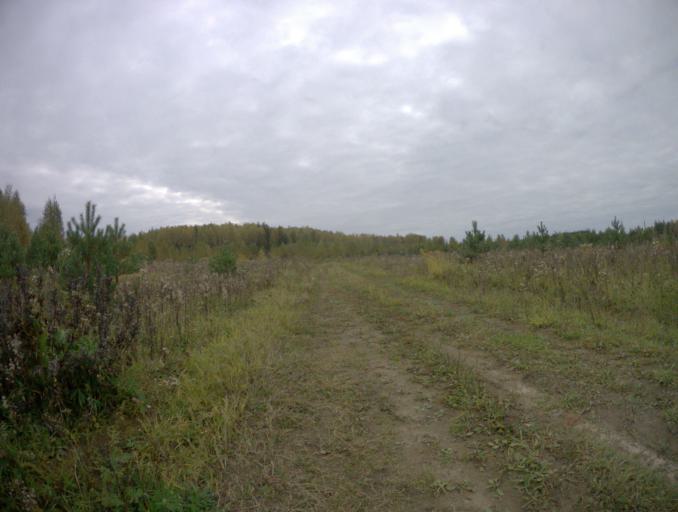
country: RU
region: Vladimir
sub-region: Kovrovskiy Rayon
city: Kovrov
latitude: 56.3442
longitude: 41.4507
